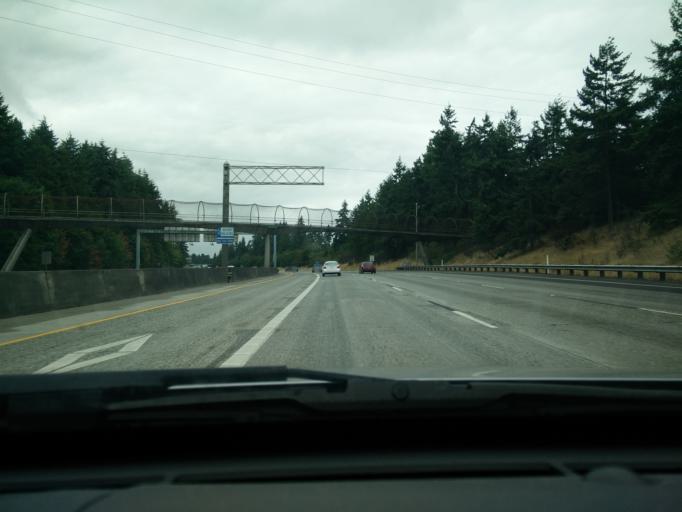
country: US
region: Washington
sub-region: Snohomish County
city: Mountlake Terrace
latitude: 47.7709
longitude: -122.3213
